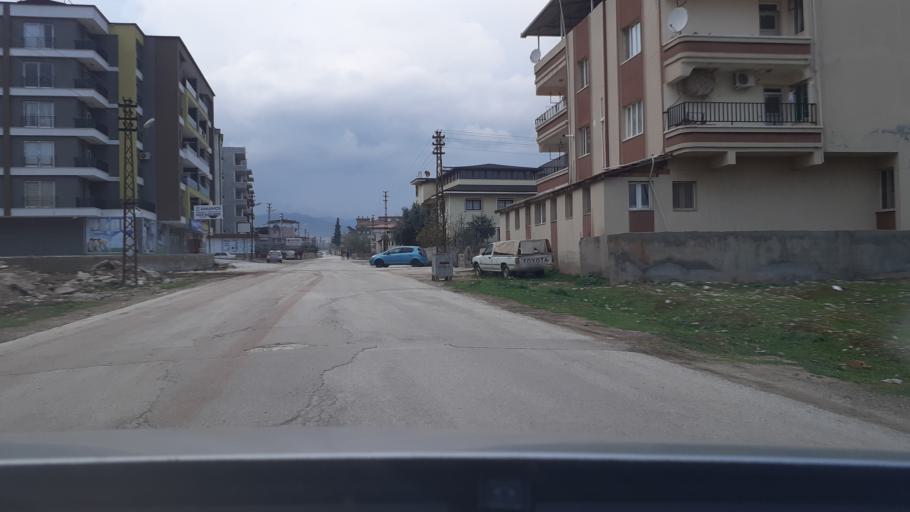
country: TR
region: Hatay
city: Kirikhan
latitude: 36.4836
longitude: 36.3555
